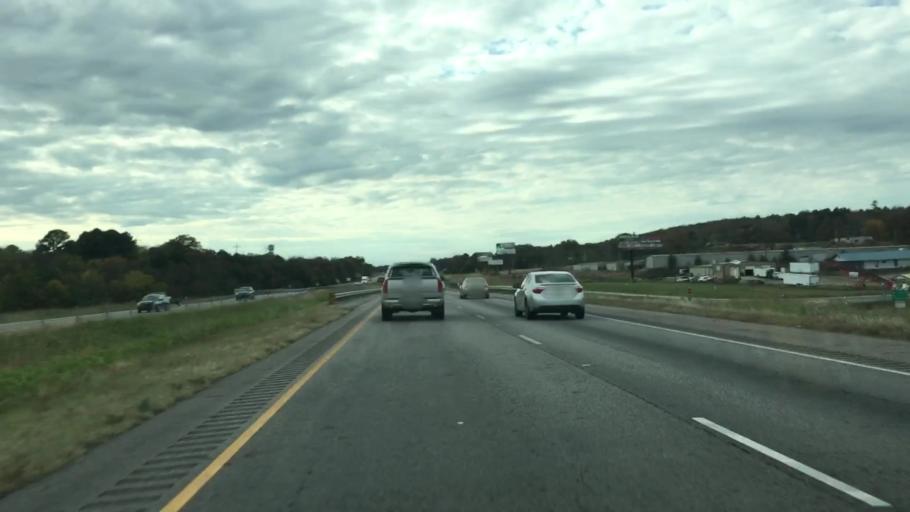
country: US
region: Arkansas
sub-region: Conway County
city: Morrilton
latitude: 35.1631
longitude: -92.6394
